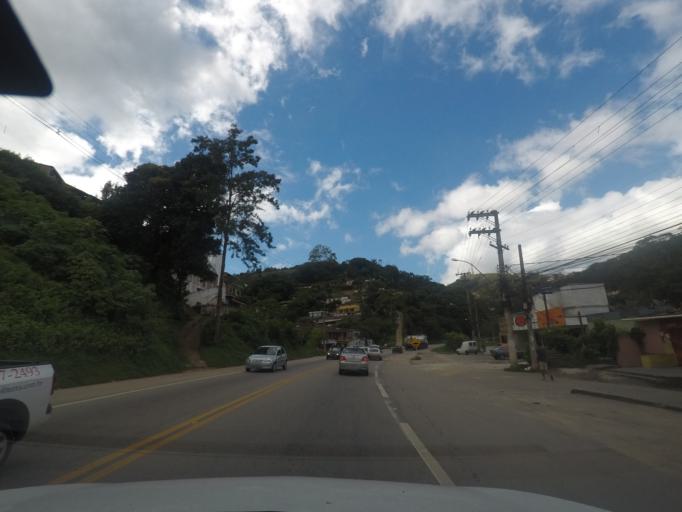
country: BR
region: Rio de Janeiro
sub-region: Teresopolis
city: Teresopolis
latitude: -22.3945
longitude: -42.9528
